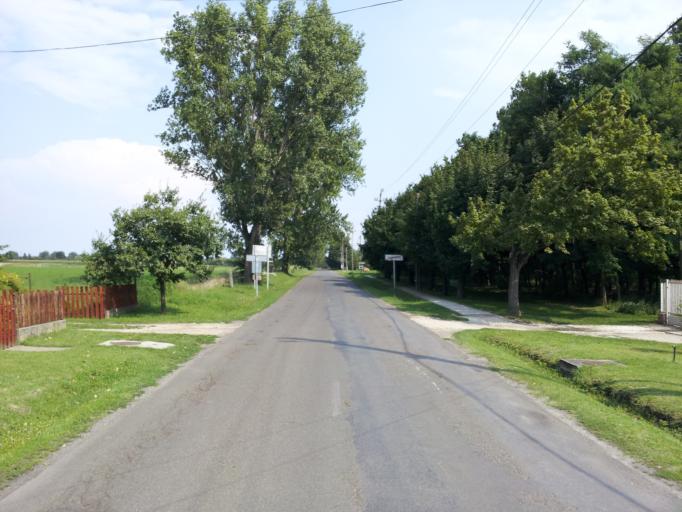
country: HU
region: Pest
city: Szigetujfalu
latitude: 47.2313
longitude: 18.9357
